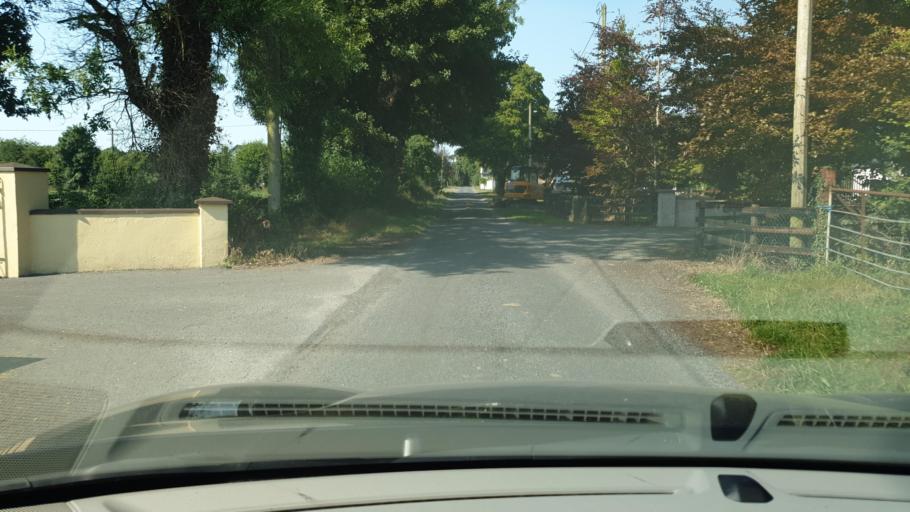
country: IE
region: Leinster
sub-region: An Mhi
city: Athboy
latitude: 53.6159
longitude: -6.9925
